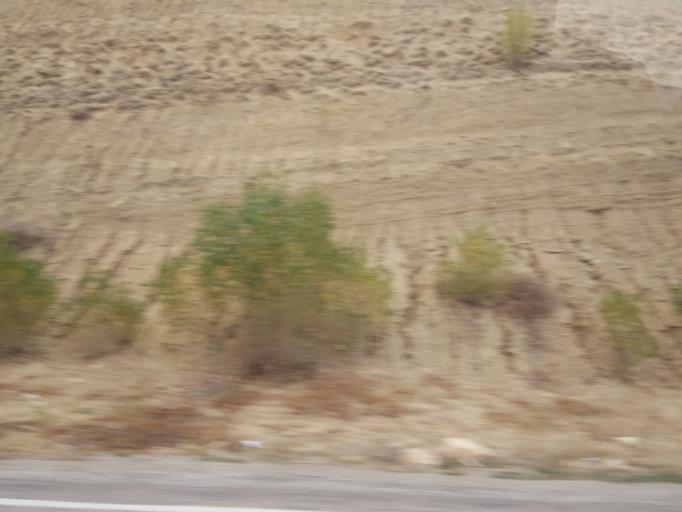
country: TR
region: Yozgat
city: Aydincik
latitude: 40.1932
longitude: 35.4049
